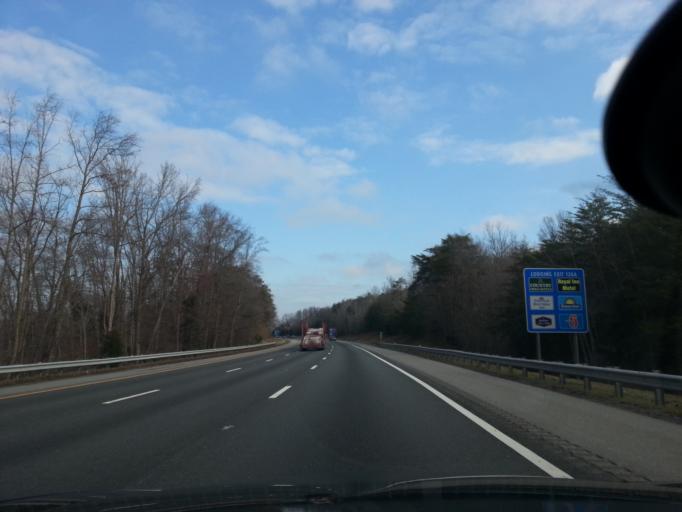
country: US
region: Virginia
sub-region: Spotsylvania County
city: Spotsylvania Courthouse
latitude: 38.2077
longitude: -77.4974
